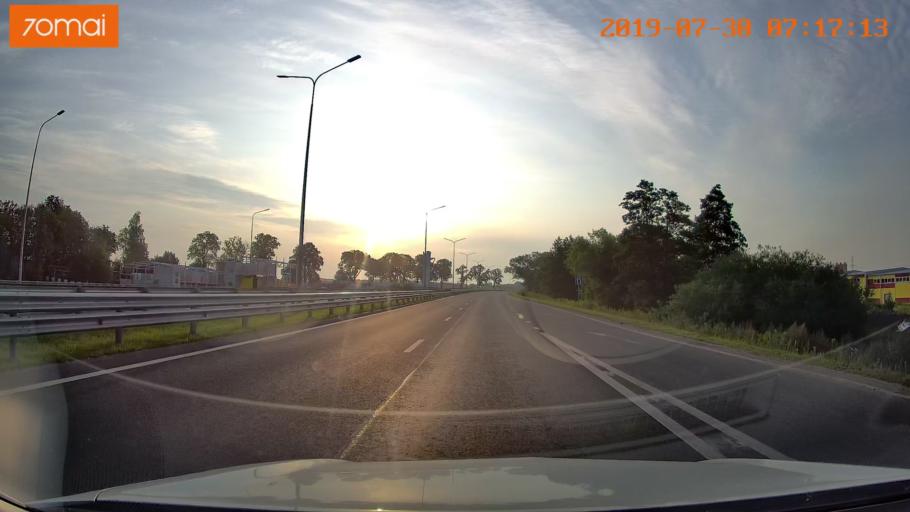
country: RU
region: Kaliningrad
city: Bol'shoe Isakovo
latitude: 54.7076
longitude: 20.6225
